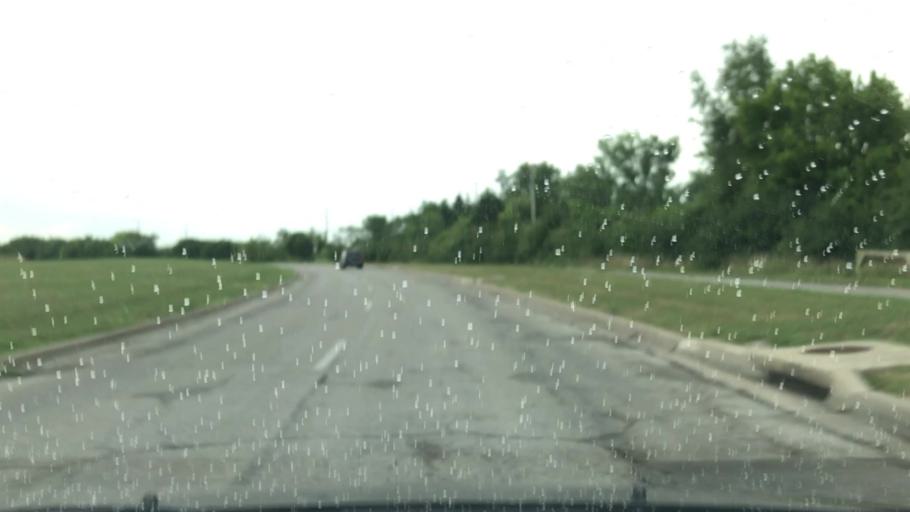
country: US
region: Missouri
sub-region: Jackson County
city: Grandview
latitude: 38.9221
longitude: -94.4836
